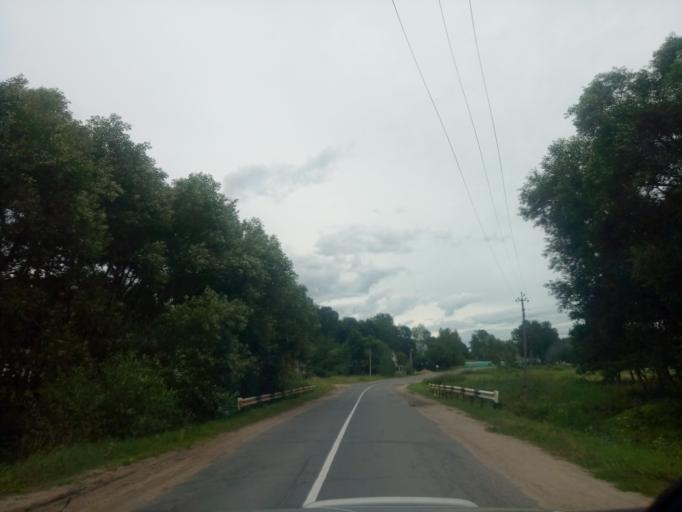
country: BY
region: Minsk
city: Zhdanovichy
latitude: 53.9241
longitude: 27.3853
